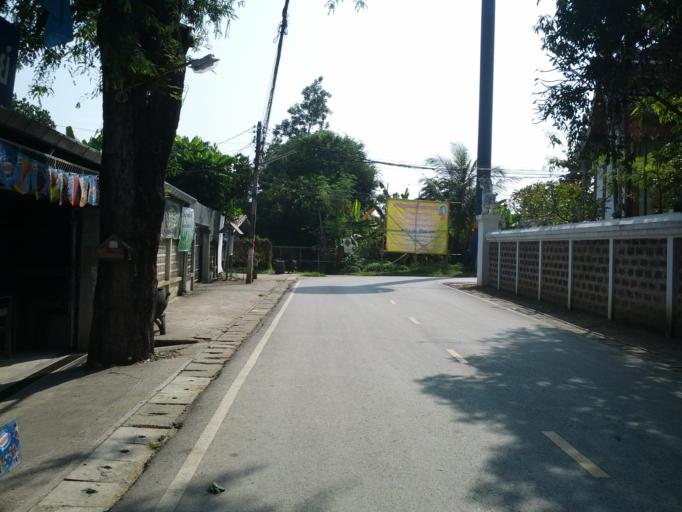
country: TH
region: Chiang Mai
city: San Kamphaeng
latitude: 18.7669
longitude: 99.0881
